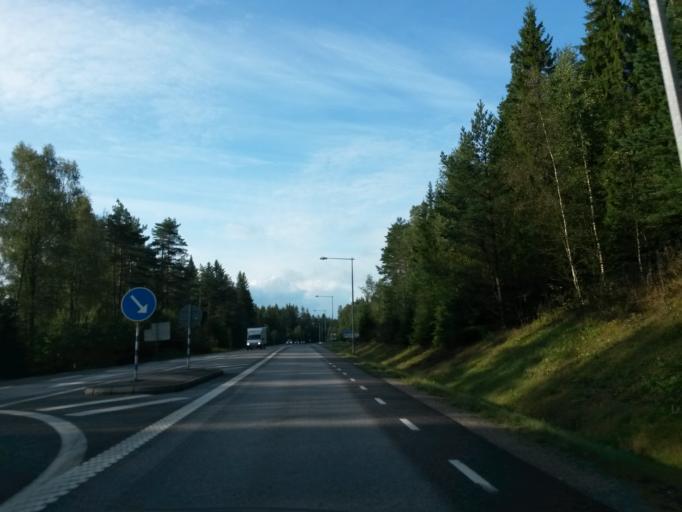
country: SE
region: Vaestra Goetaland
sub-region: Boras Kommun
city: Boras
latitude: 57.6894
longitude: 12.9431
